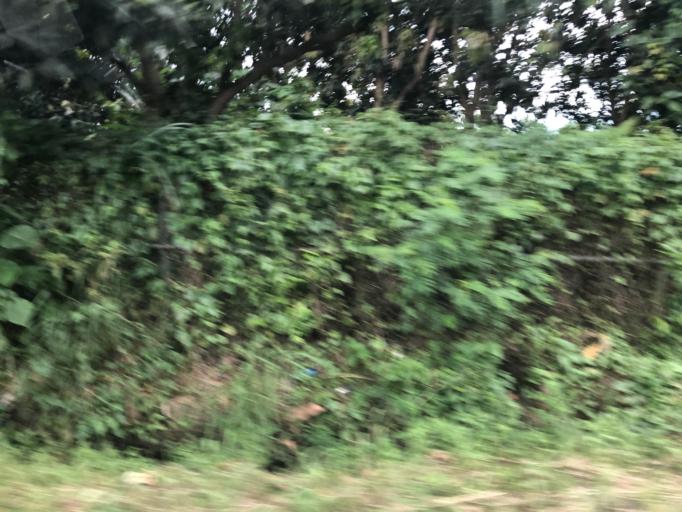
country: TW
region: Taiwan
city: Daxi
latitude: 24.9138
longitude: 121.3630
